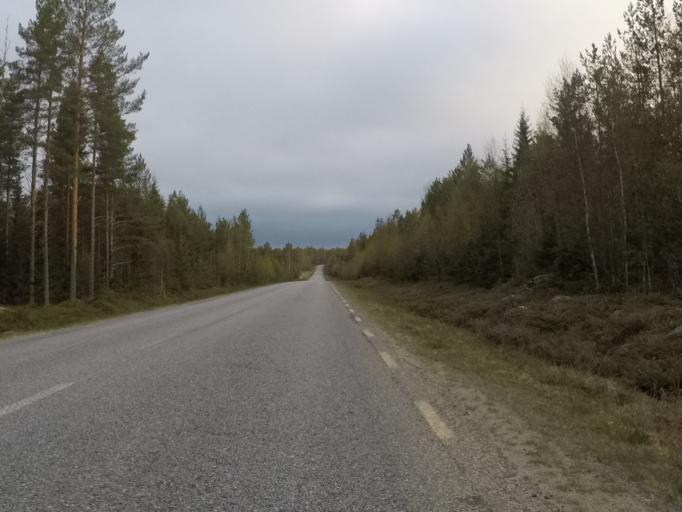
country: SE
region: Vaesterbotten
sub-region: Umea Kommun
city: Saevar
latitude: 63.9451
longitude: 20.7897
